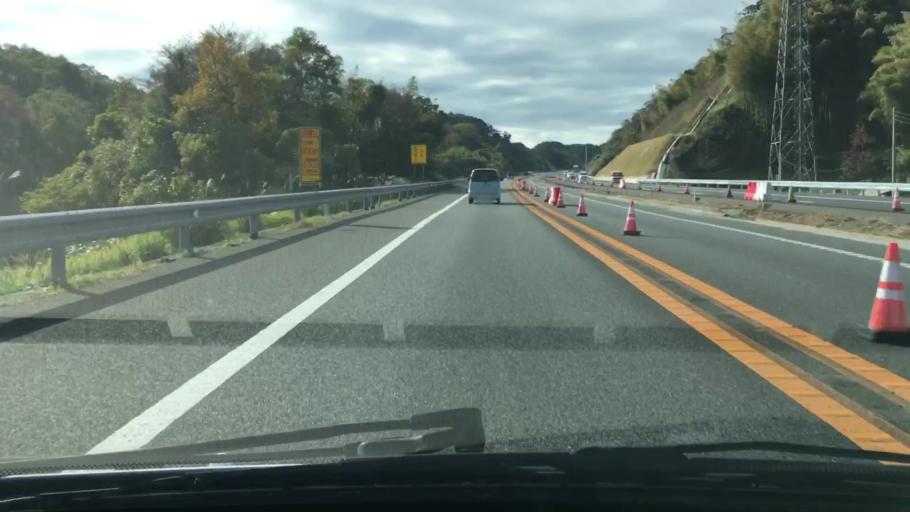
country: JP
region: Chiba
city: Kimitsu
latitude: 35.2791
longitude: 139.9242
